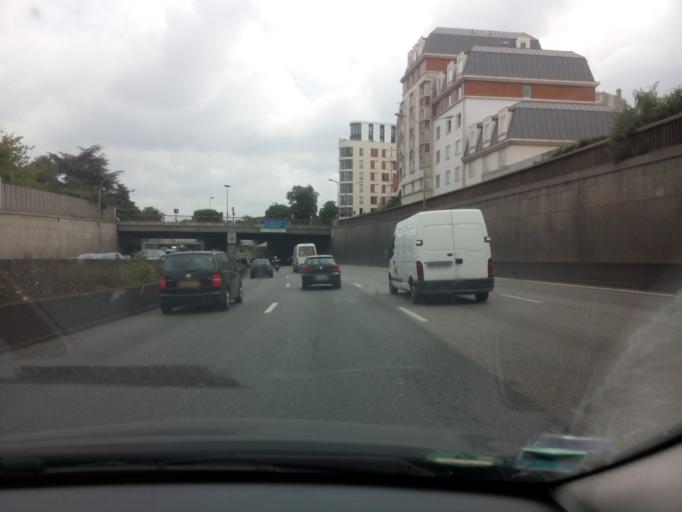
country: FR
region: Ile-de-France
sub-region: Departement du Val-de-Marne
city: Charenton-le-Pont
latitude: 48.8290
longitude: 2.3999
